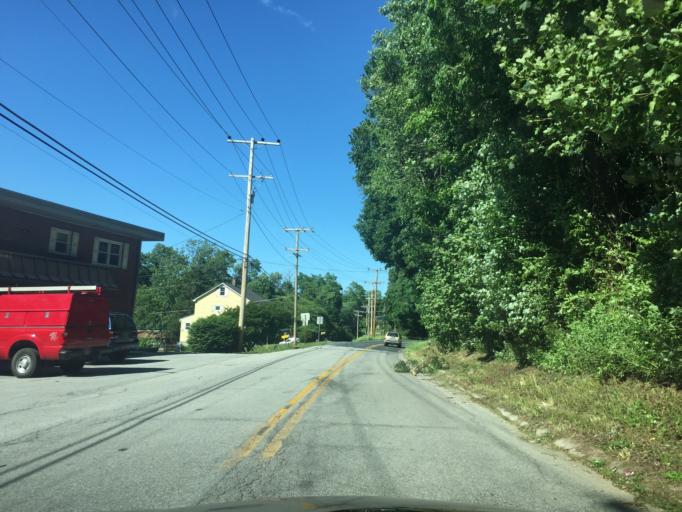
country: US
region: Maryland
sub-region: Carroll County
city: Westminster
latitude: 39.5689
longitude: -76.9848
